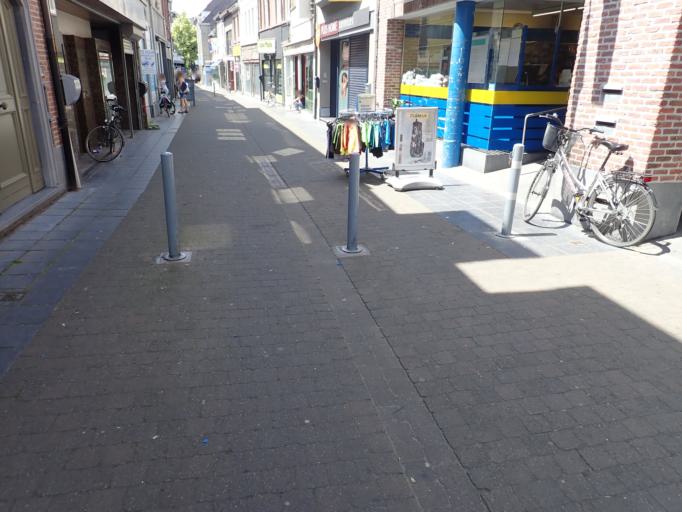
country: BE
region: Flanders
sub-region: Provincie Oost-Vlaanderen
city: Hamme
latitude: 51.0982
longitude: 4.1367
